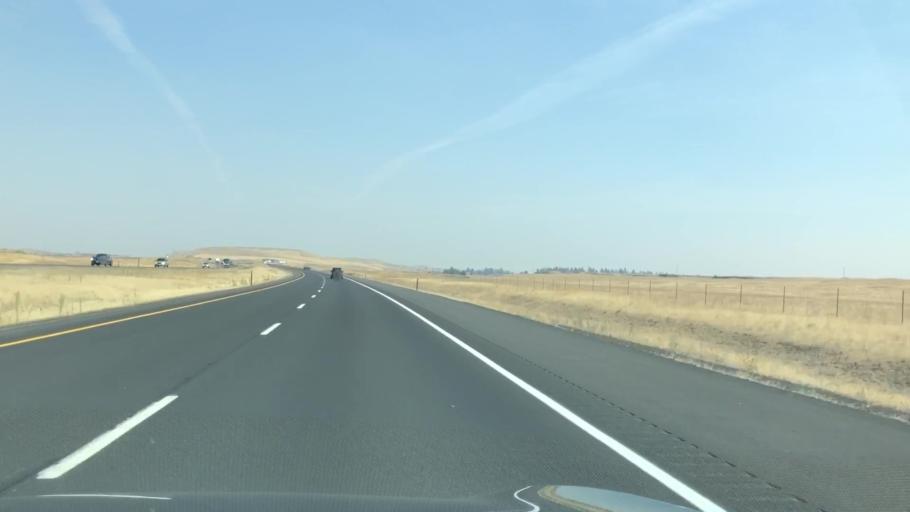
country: US
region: Washington
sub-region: Spokane County
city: Medical Lake
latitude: 47.3354
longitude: -117.9142
